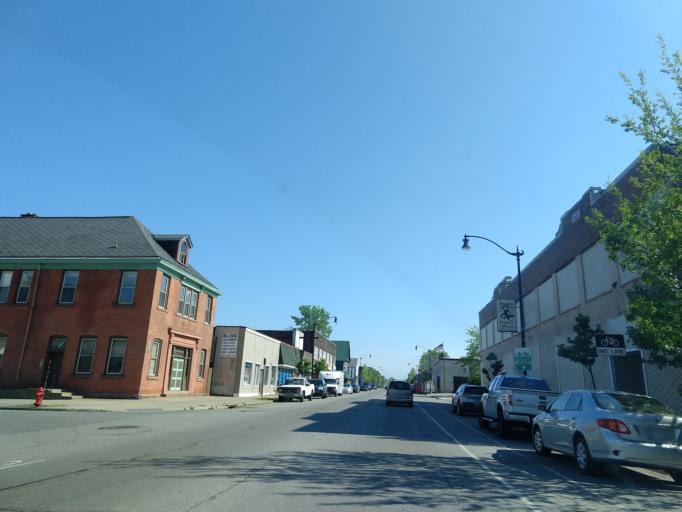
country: US
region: New York
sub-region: Erie County
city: Lackawanna
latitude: 42.8438
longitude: -78.8238
